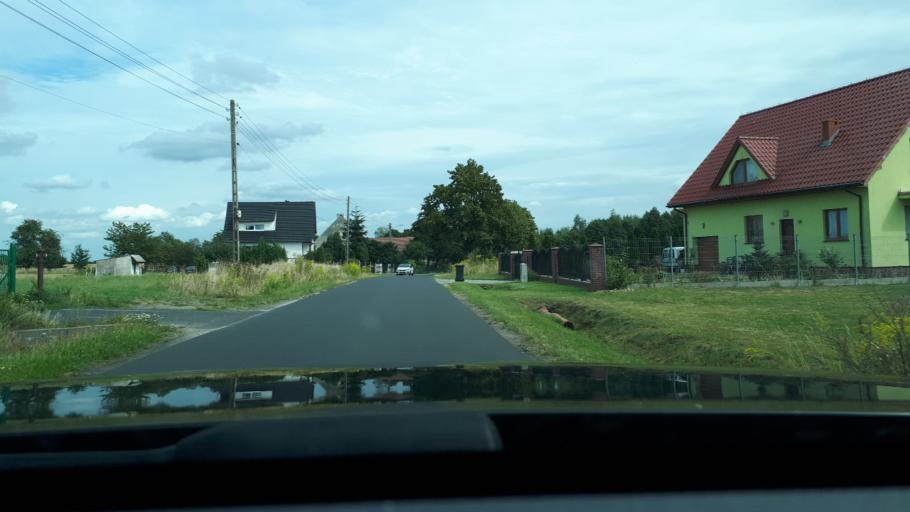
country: PL
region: Lower Silesian Voivodeship
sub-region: Powiat zlotoryjski
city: Olszanica
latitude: 51.2388
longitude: 15.8268
